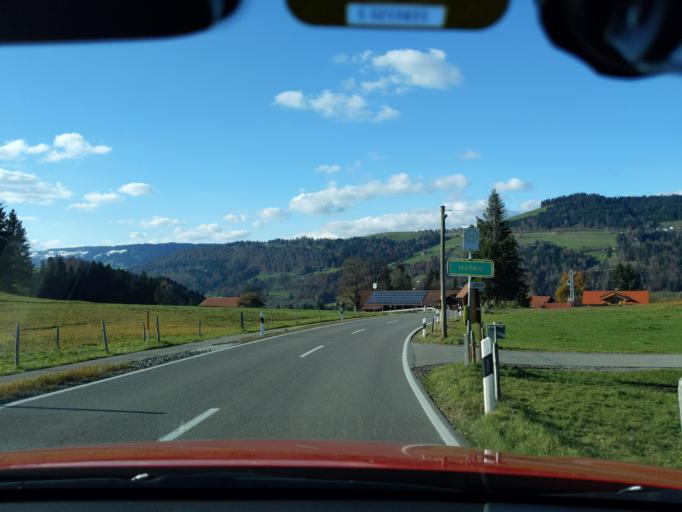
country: DE
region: Bavaria
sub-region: Swabia
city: Oberstaufen
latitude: 47.5348
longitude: 10.0236
